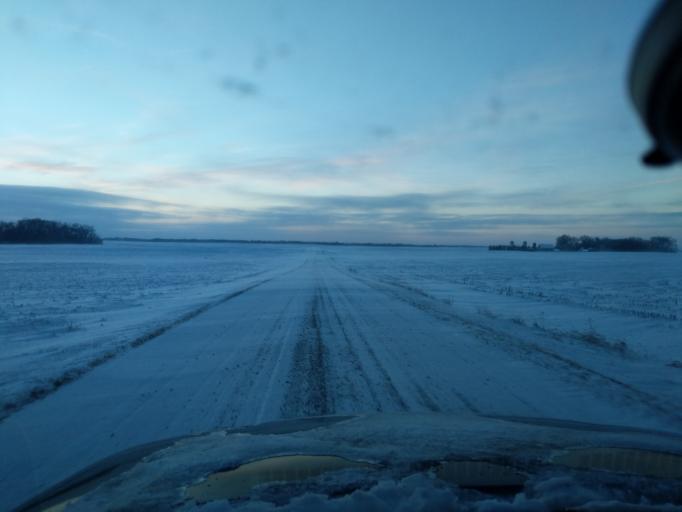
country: US
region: Minnesota
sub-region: Renville County
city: Renville
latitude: 44.7270
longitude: -95.3477
